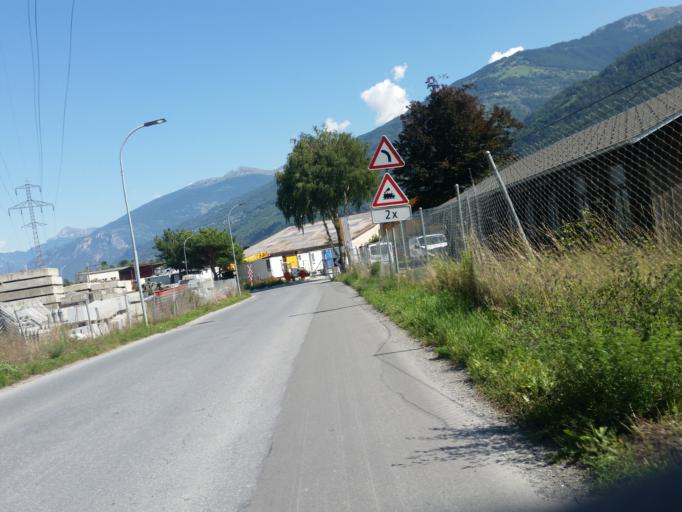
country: CH
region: Valais
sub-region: Conthey District
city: Ardon
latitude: 46.2076
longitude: 7.2762
